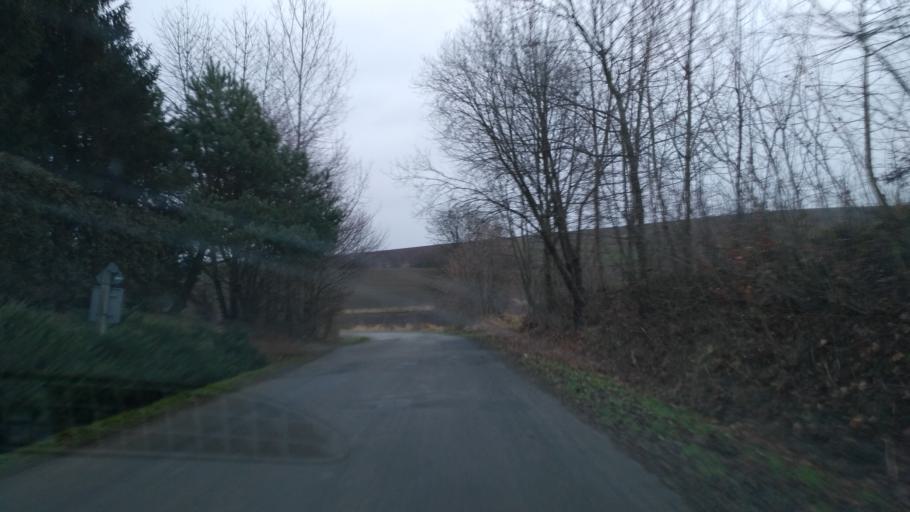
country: PL
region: Subcarpathian Voivodeship
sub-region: Powiat jaroslawski
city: Pruchnik
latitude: 49.9322
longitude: 22.5362
